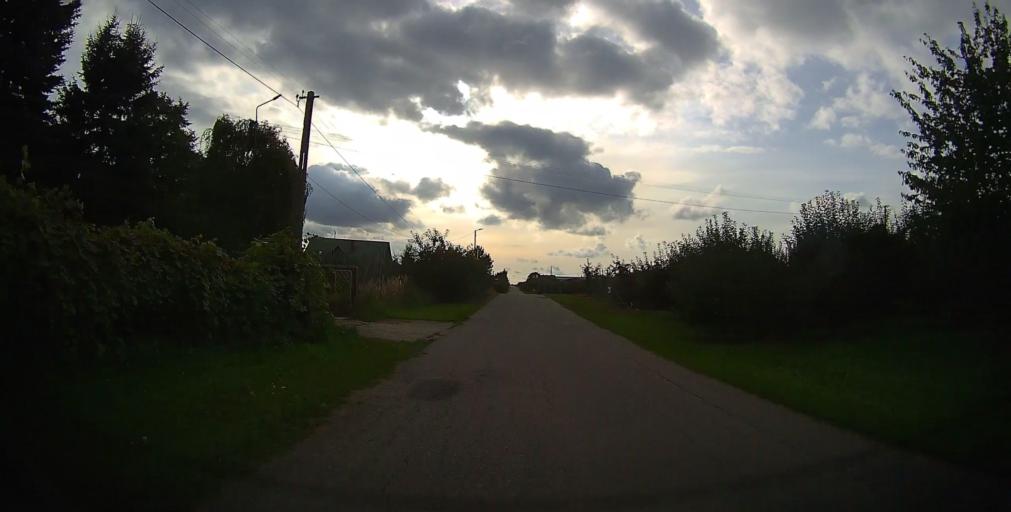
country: PL
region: Masovian Voivodeship
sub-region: Powiat grojecki
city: Jasieniec
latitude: 51.7699
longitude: 20.9104
